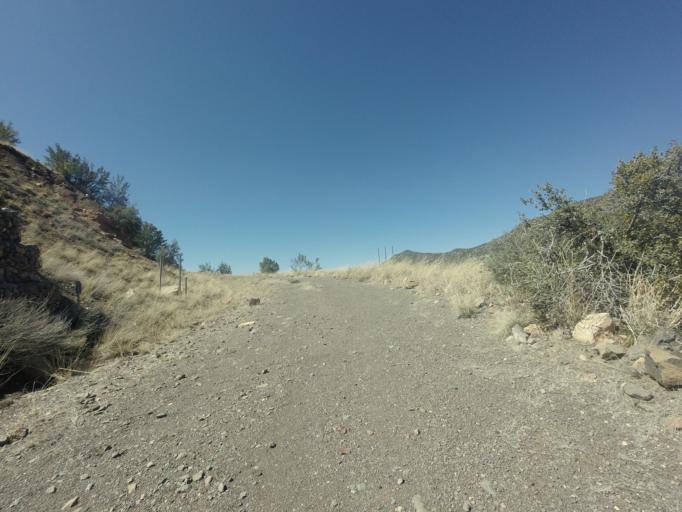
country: US
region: Arizona
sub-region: Gila County
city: Pine
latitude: 34.4055
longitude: -111.6057
